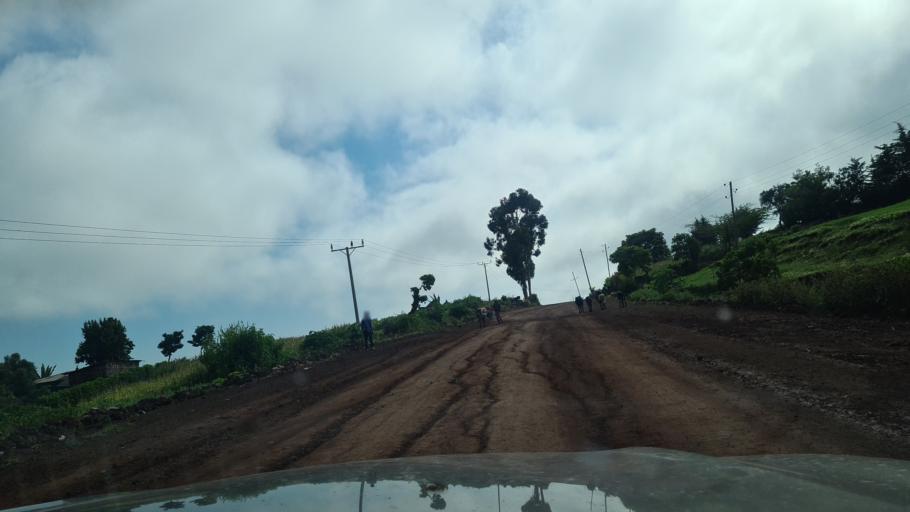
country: ET
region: Oromiya
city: Huruta
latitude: 8.1237
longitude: 39.3696
